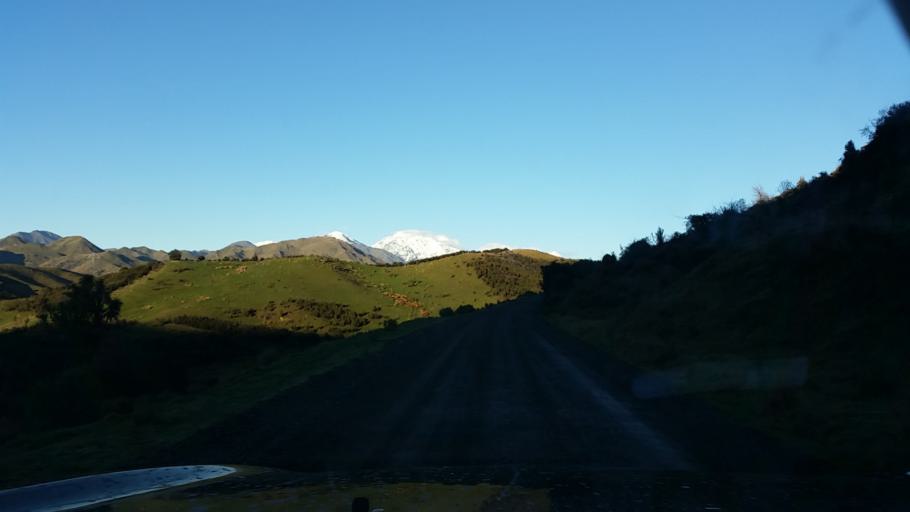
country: NZ
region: Marlborough
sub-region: Marlborough District
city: Blenheim
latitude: -41.7848
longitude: 173.7954
